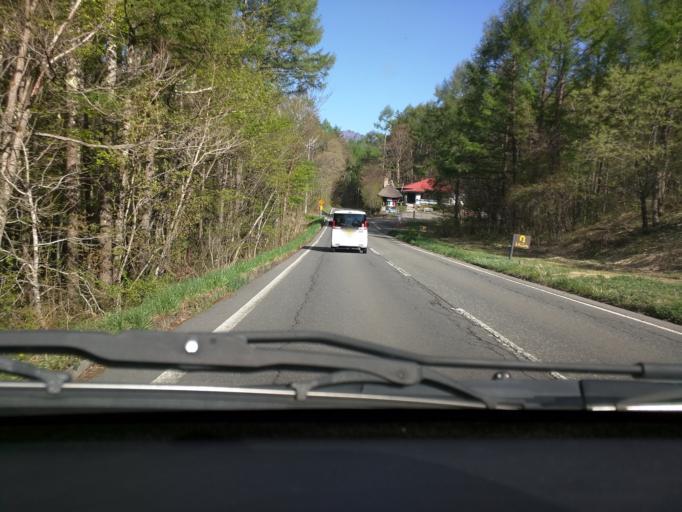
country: JP
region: Nagano
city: Nagano-shi
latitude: 36.7107
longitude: 138.1172
